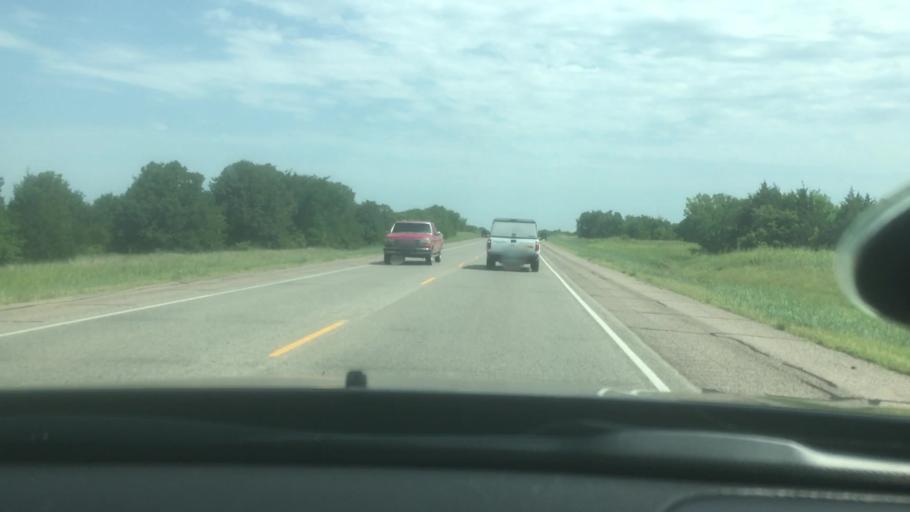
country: US
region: Oklahoma
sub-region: Seminole County
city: Maud
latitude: 35.0382
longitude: -96.9314
